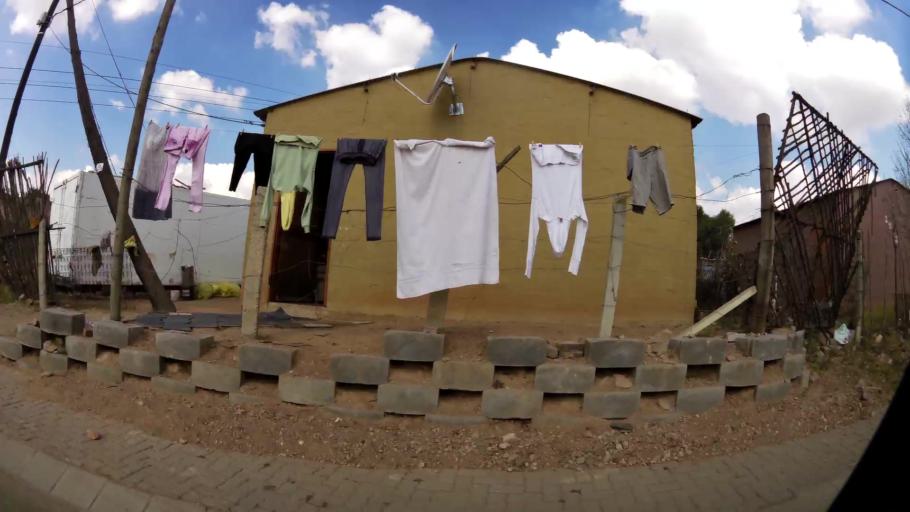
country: ZA
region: Gauteng
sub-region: City of Johannesburg Metropolitan Municipality
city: Roodepoort
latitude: -26.1837
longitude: 27.8513
